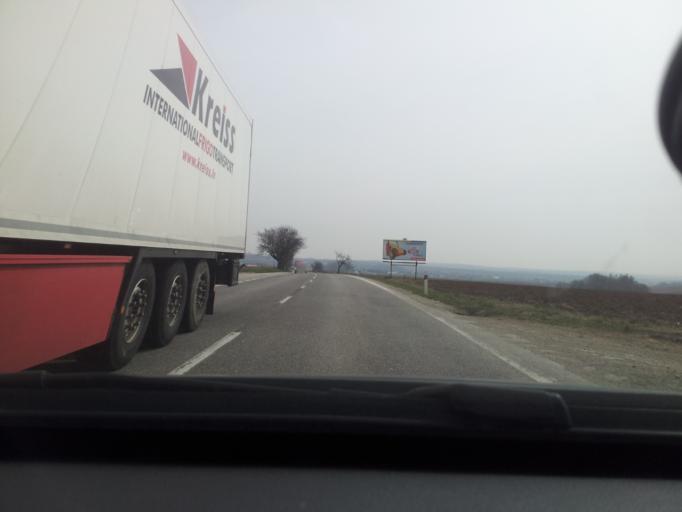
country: SK
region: Nitriansky
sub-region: Okres Nitra
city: Nitra
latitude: 48.3035
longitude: 18.1547
